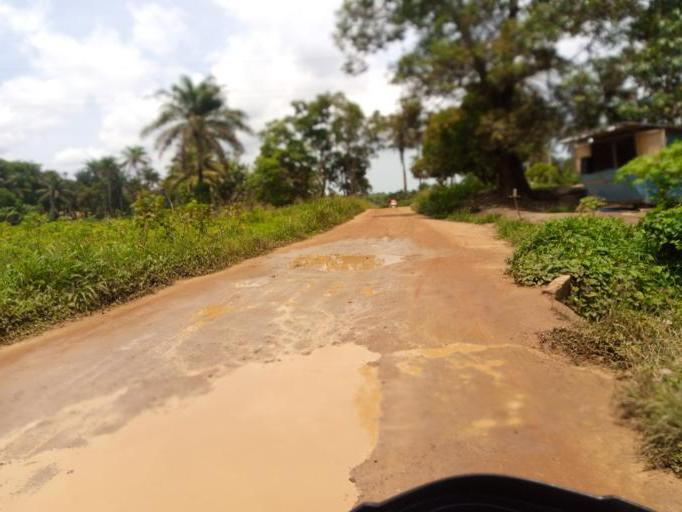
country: SL
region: Western Area
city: Waterloo
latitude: 8.3331
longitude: -13.0046
